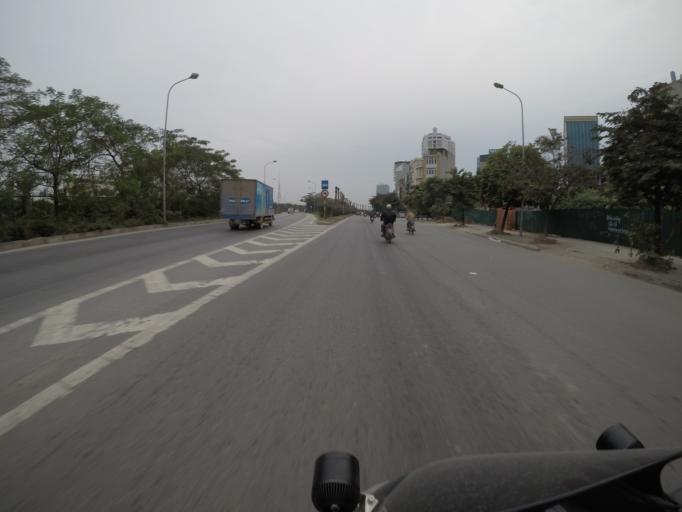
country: VN
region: Ha Noi
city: Thanh Xuan
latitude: 21.0030
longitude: 105.7812
